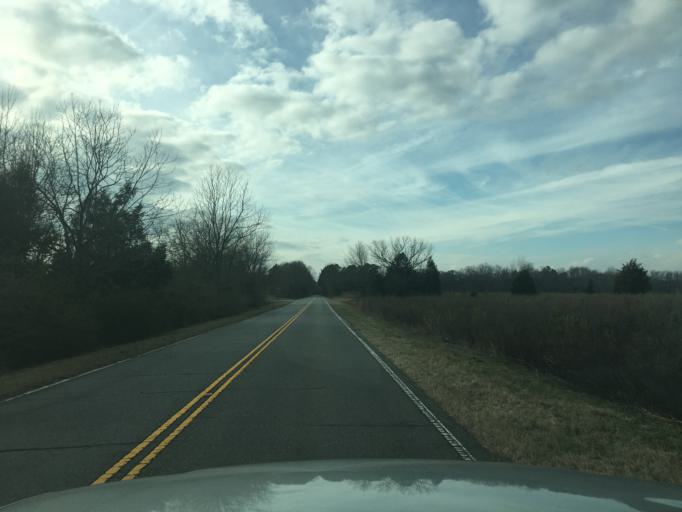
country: US
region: South Carolina
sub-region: Abbeville County
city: Lake Secession
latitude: 34.3592
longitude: -82.5122
